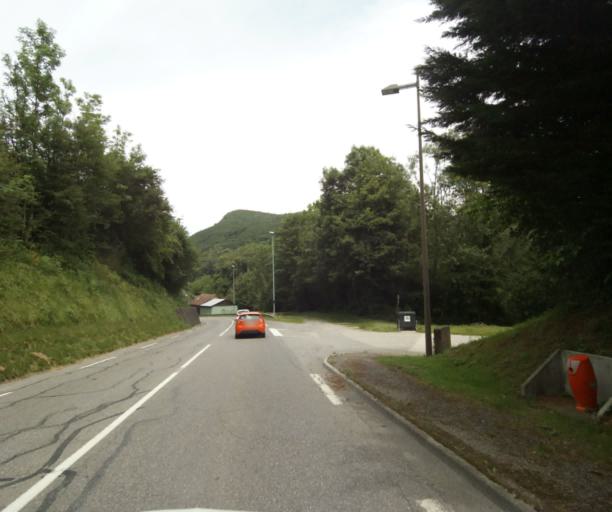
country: FR
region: Rhone-Alpes
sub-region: Departement de la Haute-Savoie
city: Perrignier
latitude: 46.3096
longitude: 6.4403
